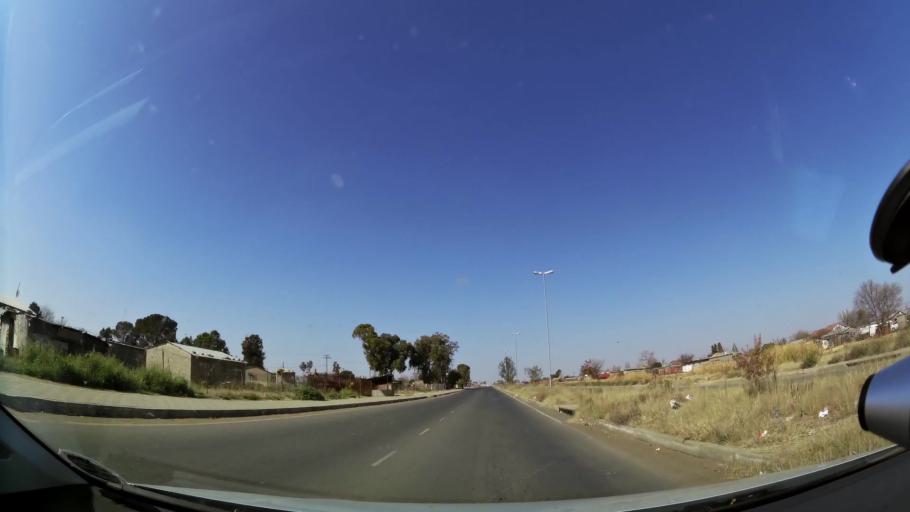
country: ZA
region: Orange Free State
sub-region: Mangaung Metropolitan Municipality
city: Bloemfontein
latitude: -29.1532
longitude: 26.2718
